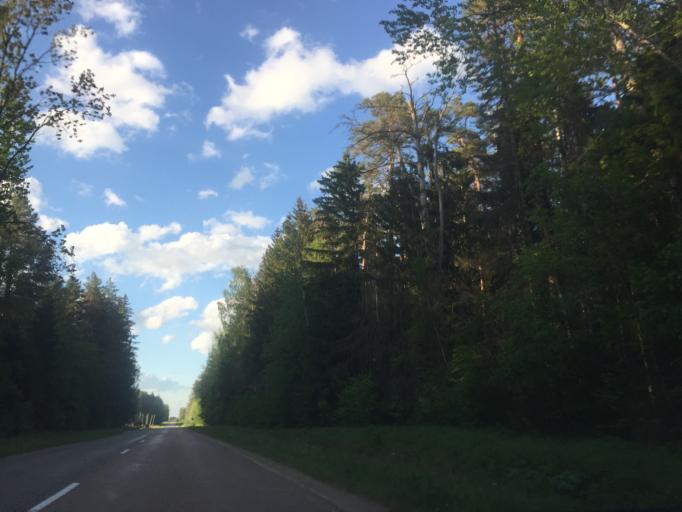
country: LV
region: Kandava
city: Kandava
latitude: 57.0066
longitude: 22.7812
